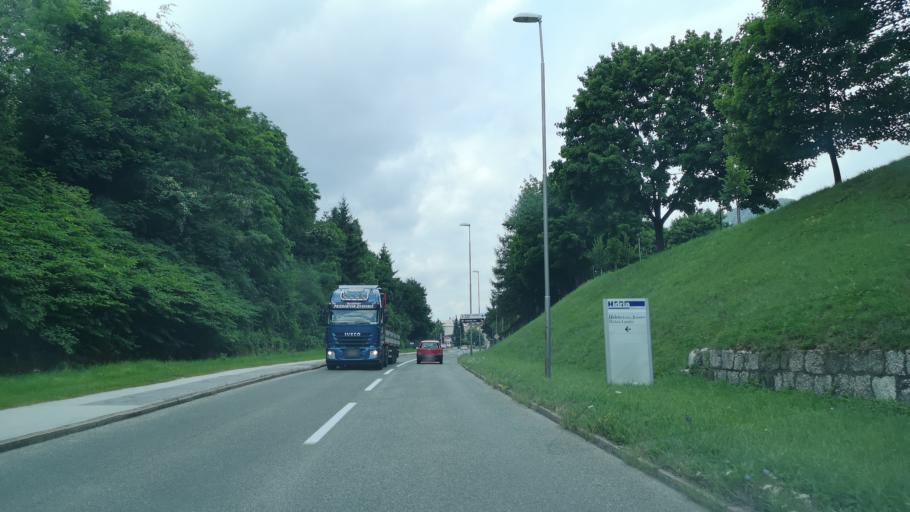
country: SI
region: Jesenice
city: Jesenice
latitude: 46.4295
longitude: 14.0761
